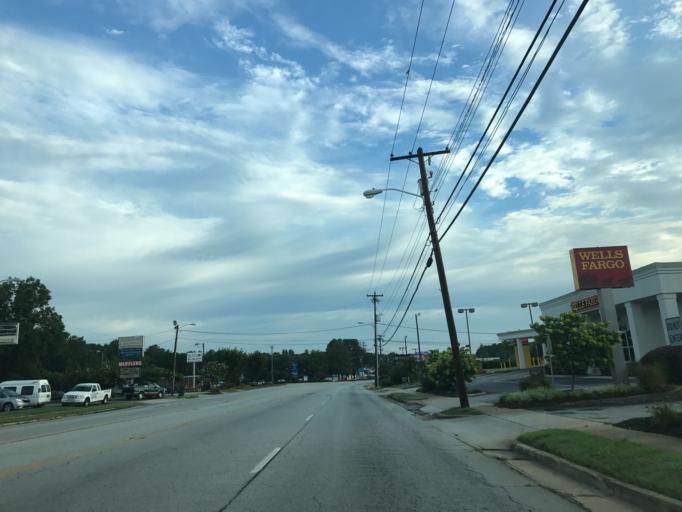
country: US
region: South Carolina
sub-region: Greenville County
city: Mauldin
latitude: 34.7848
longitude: -82.3126
